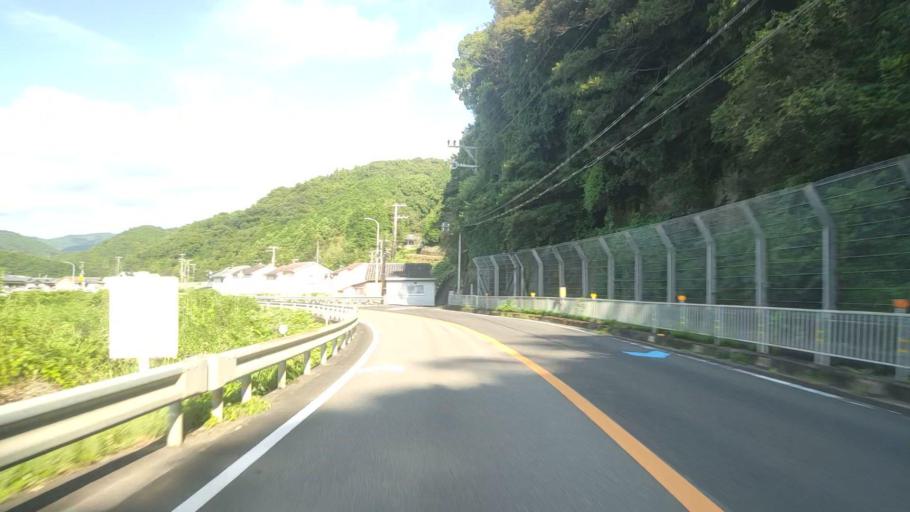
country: JP
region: Wakayama
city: Tanabe
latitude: 33.6634
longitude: 135.4038
